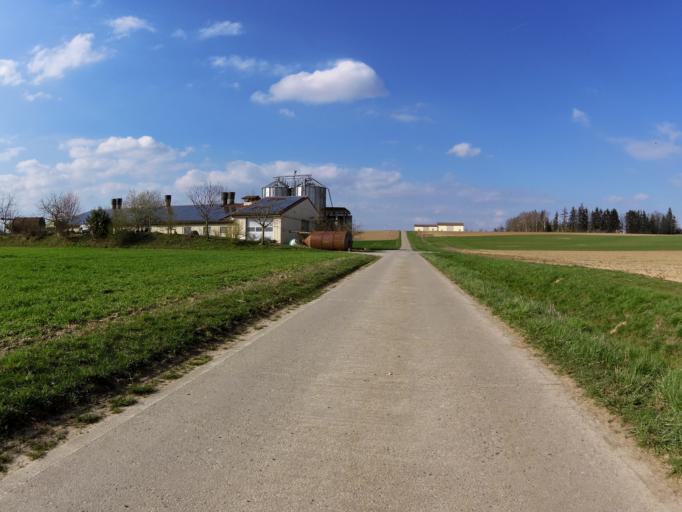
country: DE
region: Bavaria
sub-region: Regierungsbezirk Unterfranken
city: Biebelried
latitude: 49.7913
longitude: 10.0803
